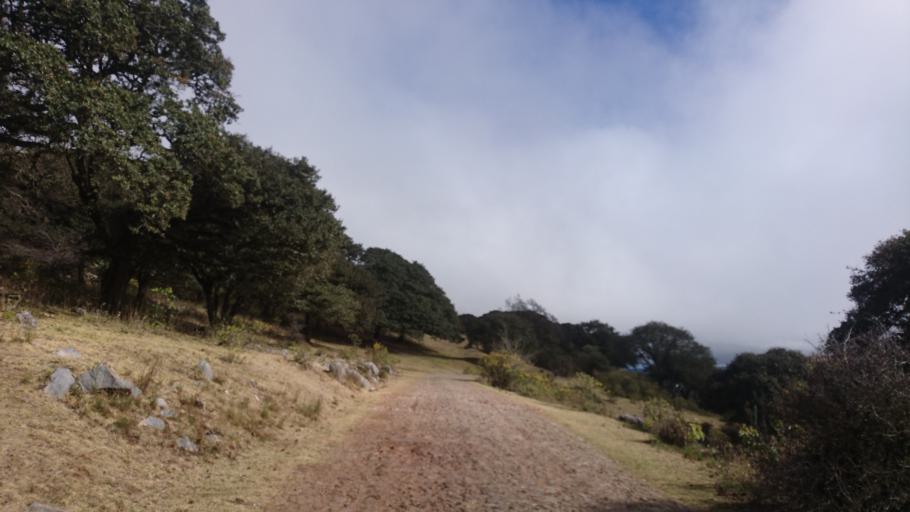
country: MX
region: San Luis Potosi
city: Zaragoza
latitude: 22.0668
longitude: -100.6440
